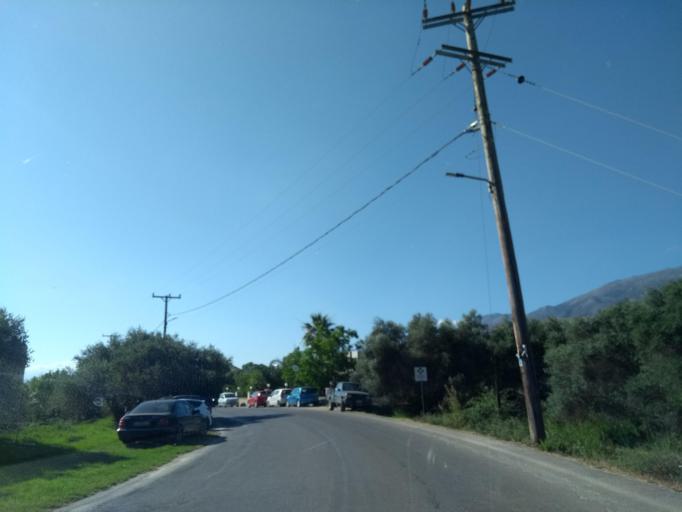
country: GR
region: Crete
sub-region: Nomos Chanias
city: Georgioupolis
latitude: 35.3677
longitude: 24.2540
